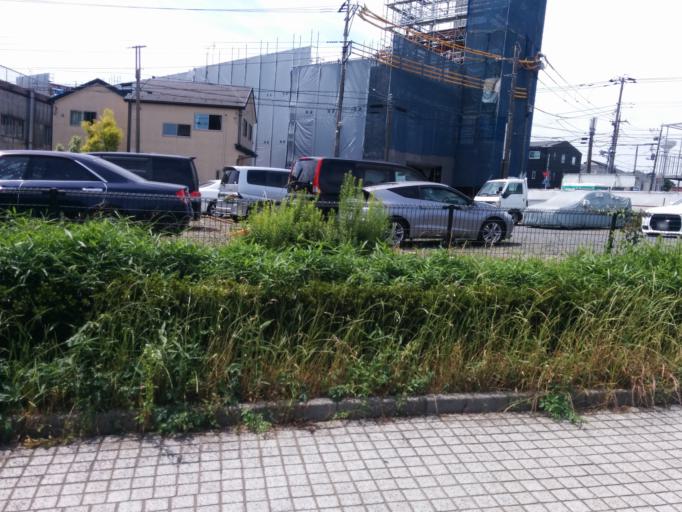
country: JP
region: Tokyo
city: Higashimurayama-shi
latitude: 35.7673
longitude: 139.4897
